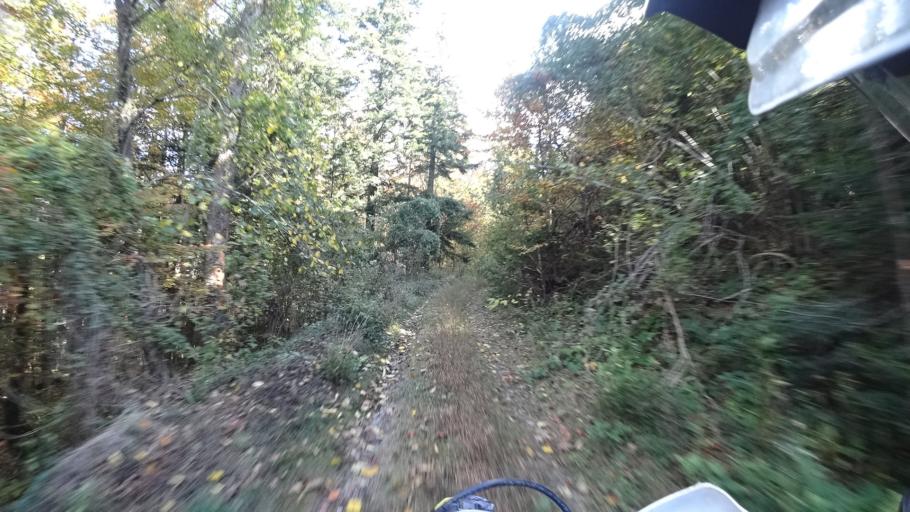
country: HR
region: Karlovacka
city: Plaski
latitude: 45.0720
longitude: 15.3214
